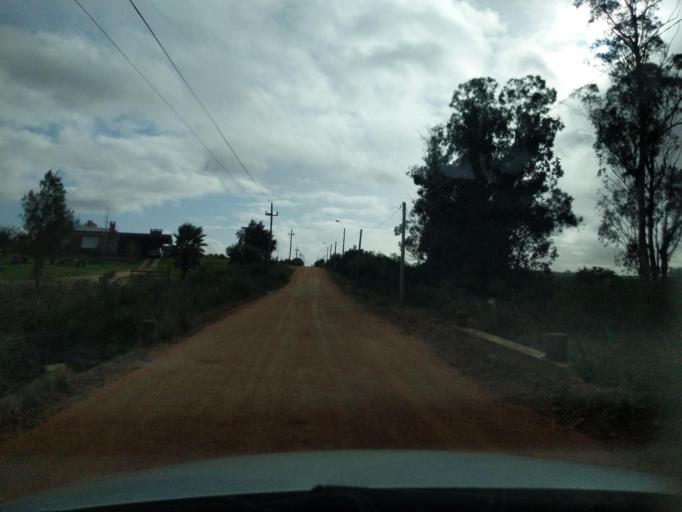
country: UY
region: Florida
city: Florida
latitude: -34.0670
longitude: -56.2191
